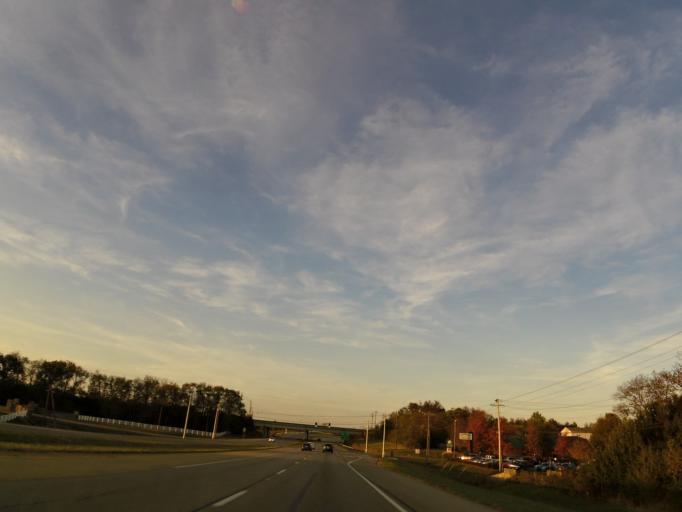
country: US
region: Kentucky
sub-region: Jessamine County
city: Nicholasville
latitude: 37.8761
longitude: -84.5972
